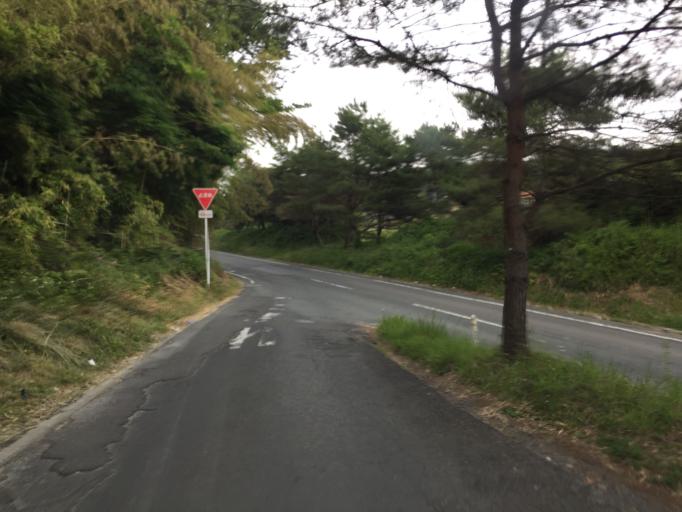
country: JP
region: Miyagi
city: Marumori
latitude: 37.7724
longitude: 140.9363
